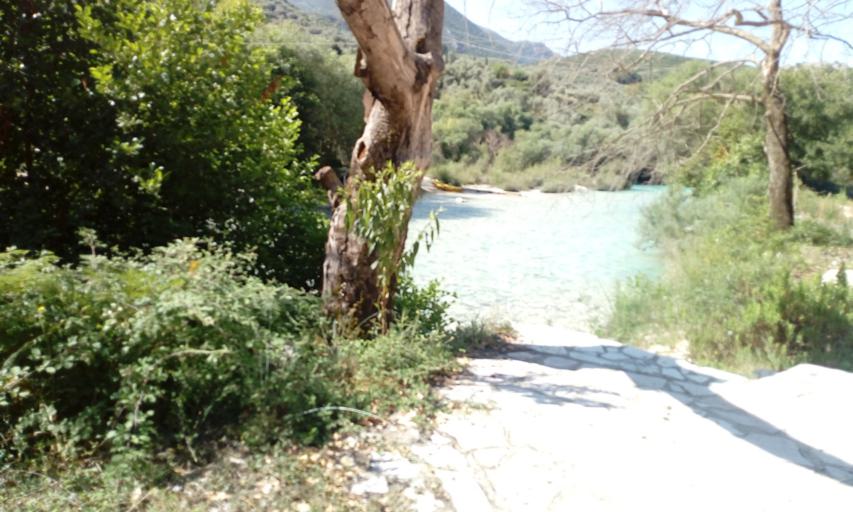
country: GR
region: Epirus
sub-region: Nomos Prevezis
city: Kanalaki
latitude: 39.3281
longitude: 20.6195
